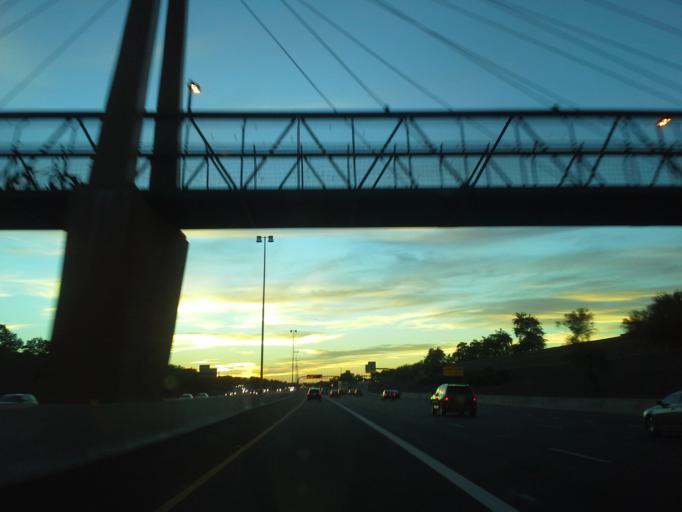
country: US
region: Arizona
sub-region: Maricopa County
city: Peoria
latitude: 33.6683
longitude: -112.1947
